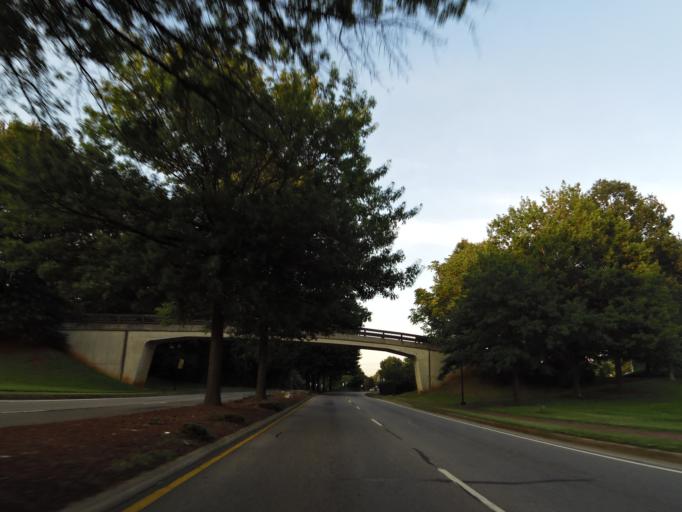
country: US
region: Tennessee
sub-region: Blount County
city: Maryville
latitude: 35.7544
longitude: -83.9673
